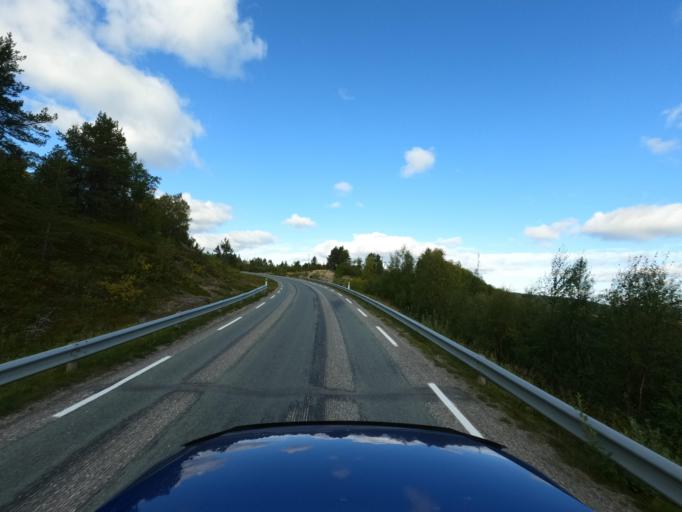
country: NO
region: Finnmark Fylke
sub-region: Karasjok
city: Karasjohka
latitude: 69.4290
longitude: 25.7938
